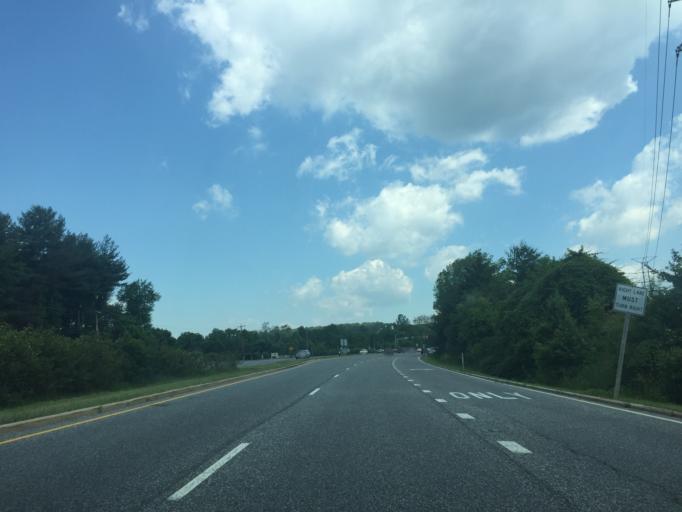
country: US
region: Maryland
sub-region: Baltimore County
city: Mays Chapel
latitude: 39.4163
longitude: -76.6675
